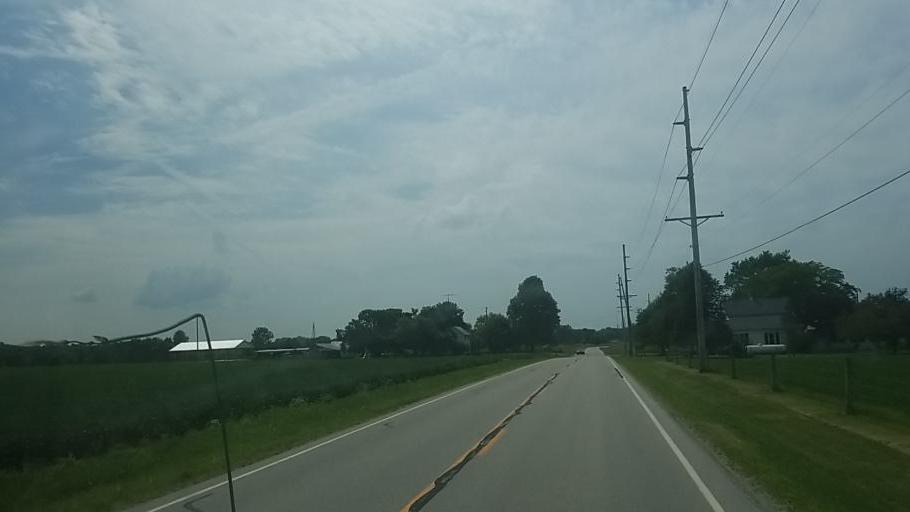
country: US
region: Ohio
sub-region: Hardin County
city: Forest
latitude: 40.7820
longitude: -83.5603
